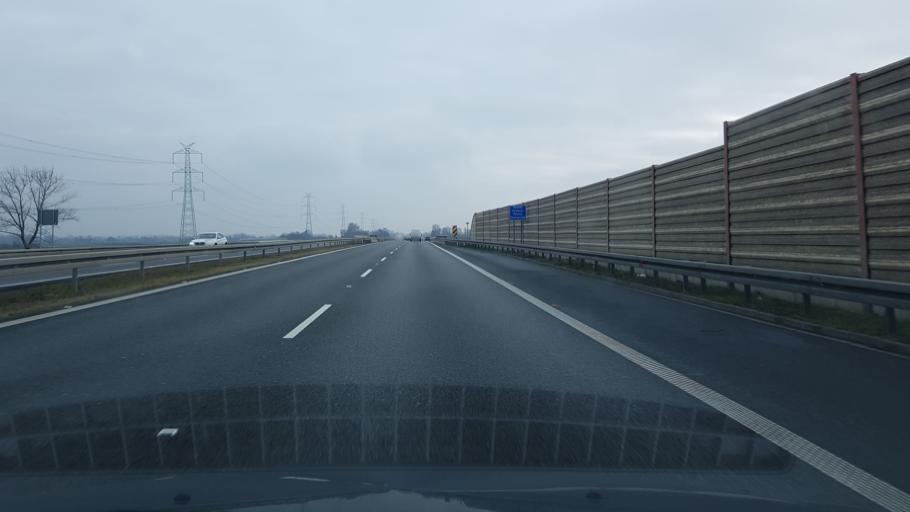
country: PL
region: Lower Silesian Voivodeship
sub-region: Powiat olawski
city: Wierzbno
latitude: 50.9336
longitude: 17.1137
